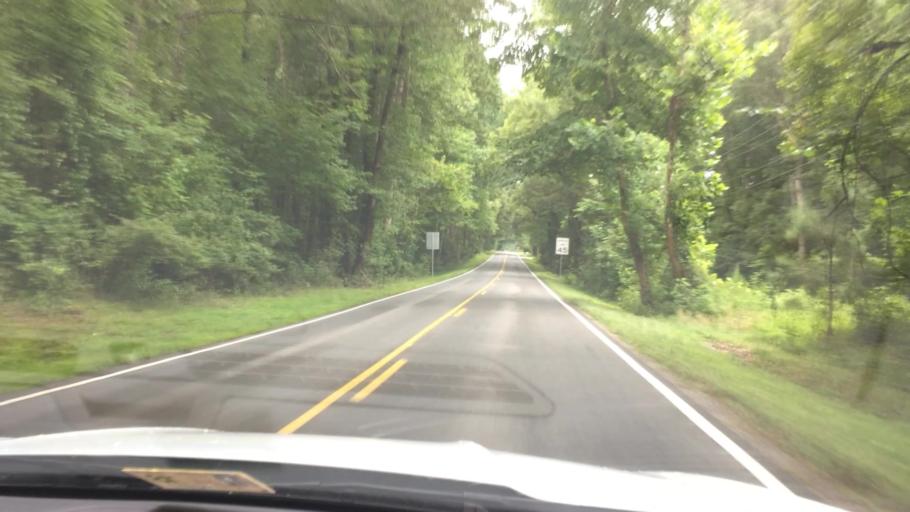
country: US
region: Virginia
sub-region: New Kent County
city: New Kent
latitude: 37.4623
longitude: -77.0349
